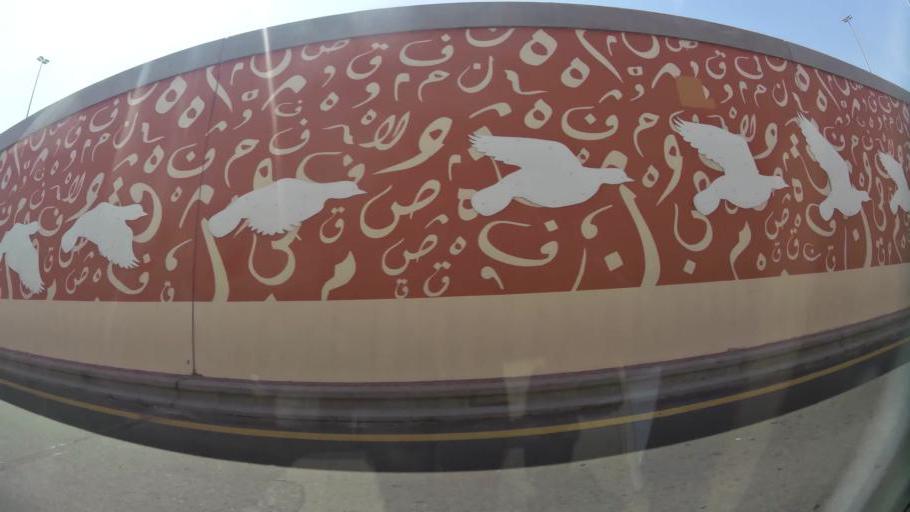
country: AE
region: Ash Shariqah
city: Sharjah
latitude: 25.2827
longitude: 55.3567
